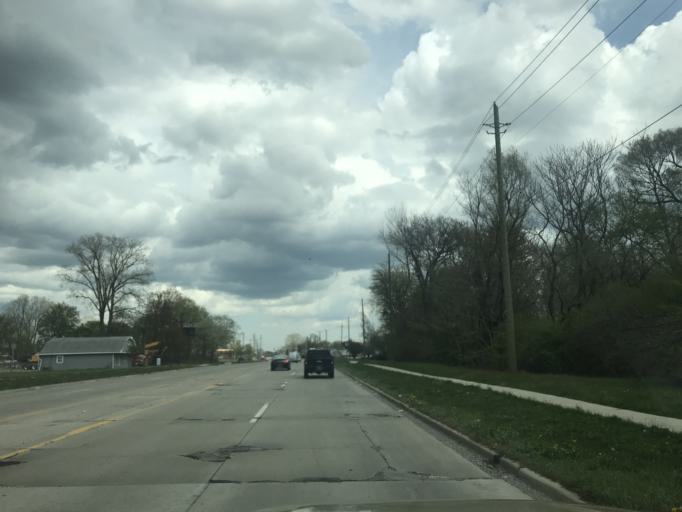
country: US
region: Michigan
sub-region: Wayne County
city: Taylor
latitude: 42.1957
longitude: -83.3106
